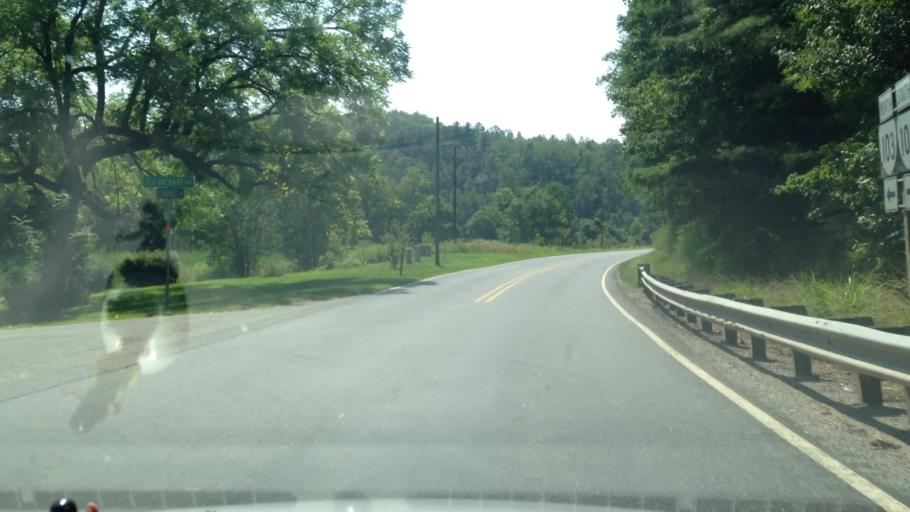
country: US
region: Virginia
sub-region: Patrick County
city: Stuart
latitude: 36.5833
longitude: -80.3842
